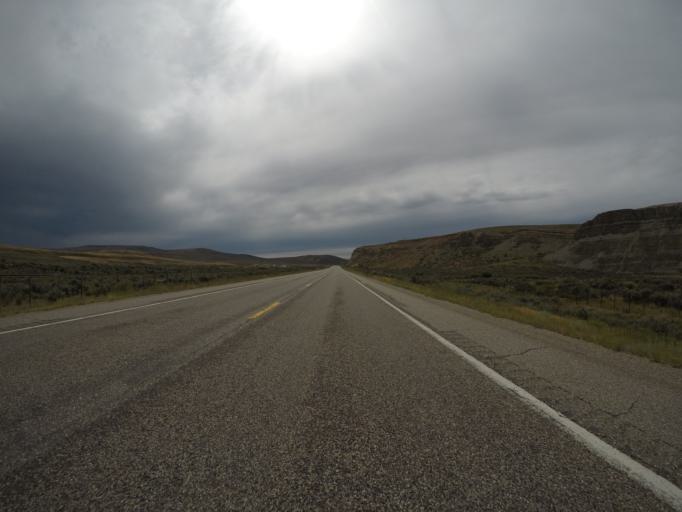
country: US
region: Utah
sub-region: Rich County
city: Randolph
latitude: 41.8228
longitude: -110.8800
